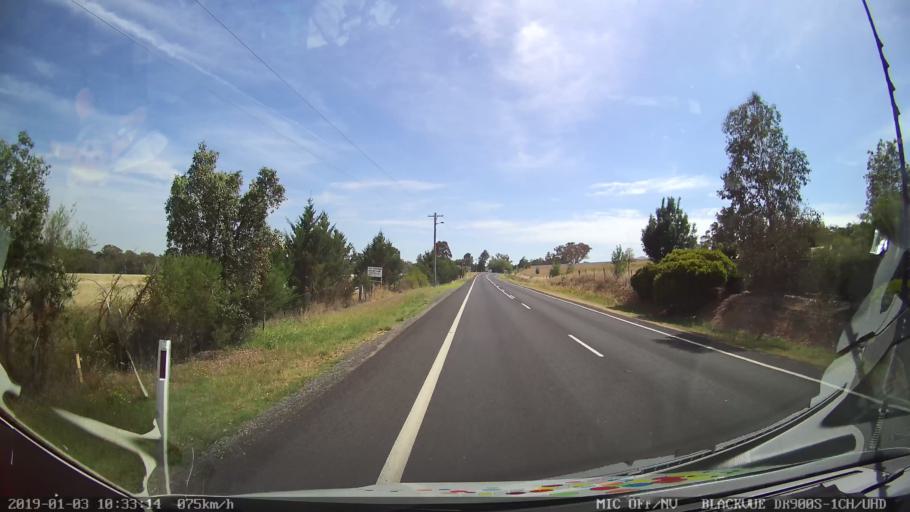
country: AU
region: New South Wales
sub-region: Young
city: Young
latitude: -34.3303
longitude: 148.2863
